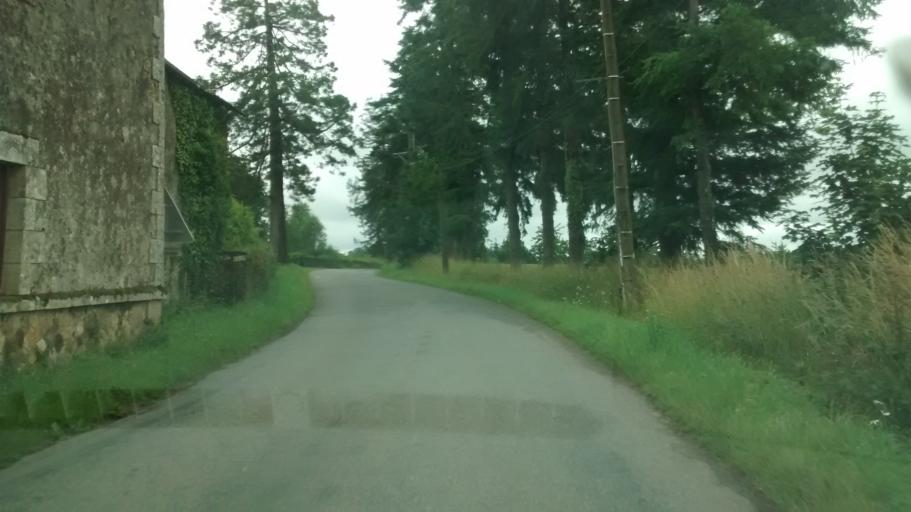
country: FR
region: Brittany
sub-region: Departement du Morbihan
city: Serent
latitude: 47.7976
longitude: -2.4591
